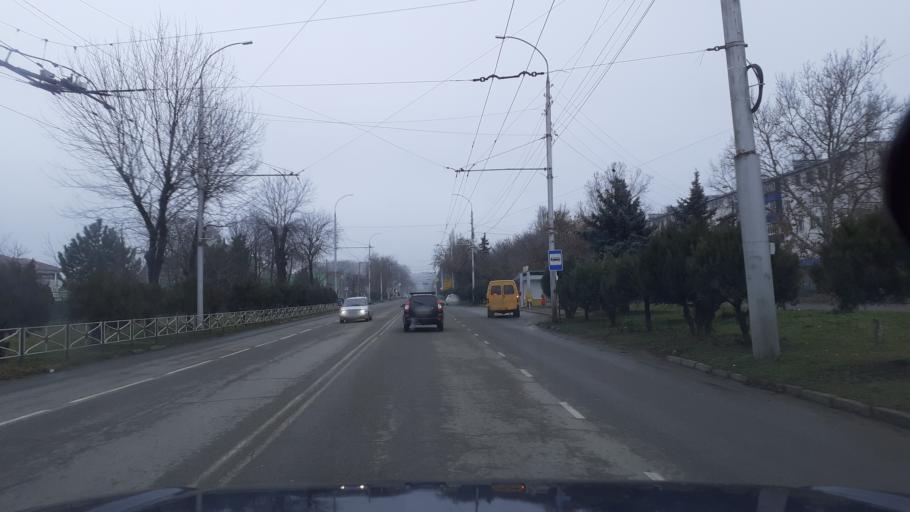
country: RU
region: Adygeya
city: Maykop
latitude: 44.6186
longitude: 40.0639
